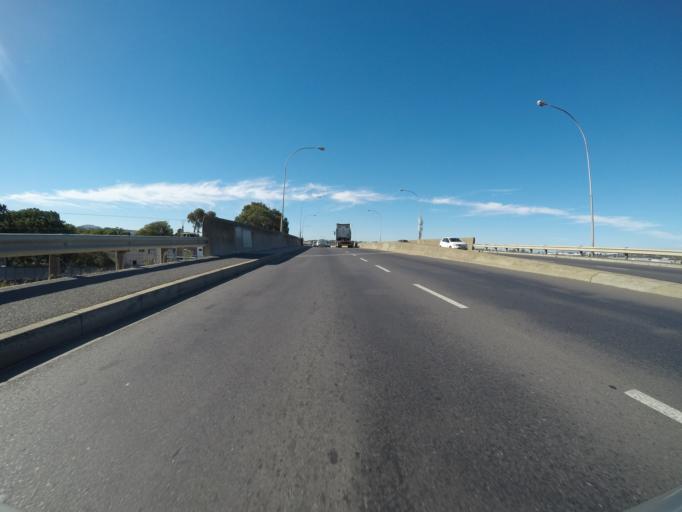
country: ZA
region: Western Cape
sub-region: City of Cape Town
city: Kraaifontein
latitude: -33.8935
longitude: 18.6725
